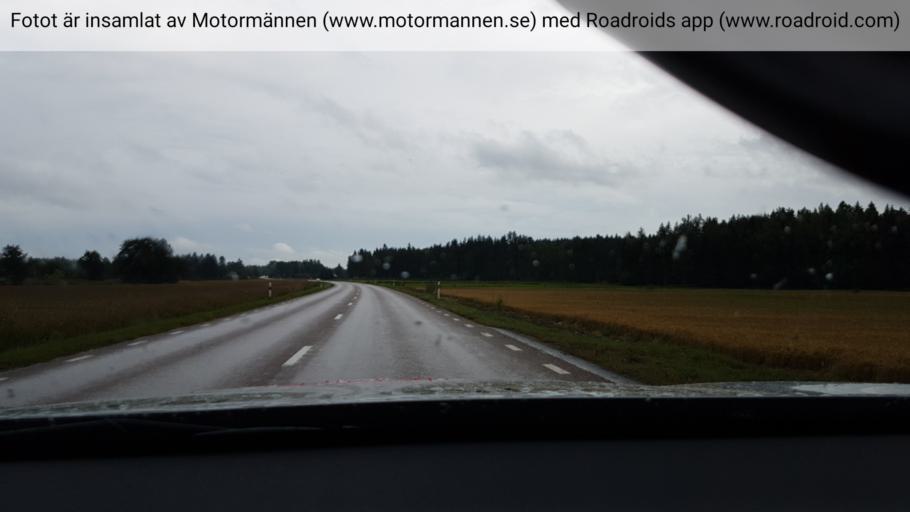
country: SE
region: Uppsala
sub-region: Tierps Kommun
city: Karlholmsbruk
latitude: 60.4508
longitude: 17.7709
